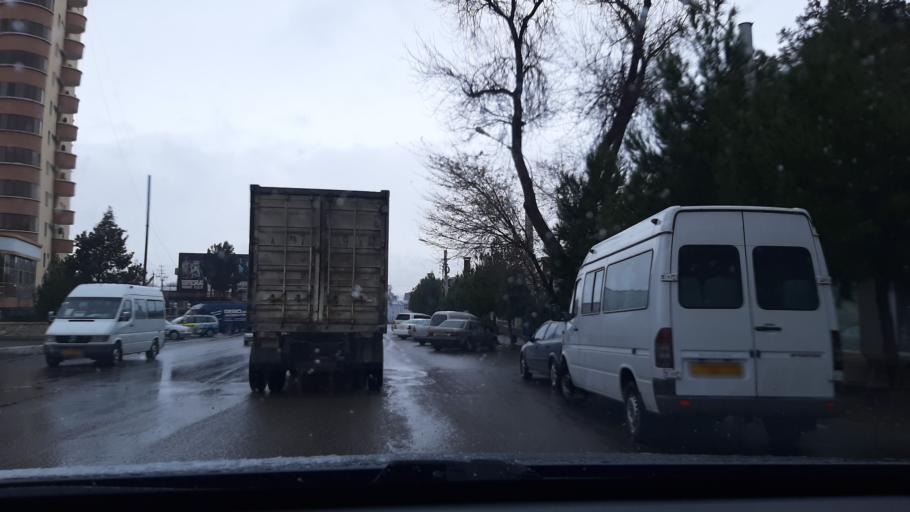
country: TJ
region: Viloyati Sughd
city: Khujand
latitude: 40.2727
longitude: 69.6429
